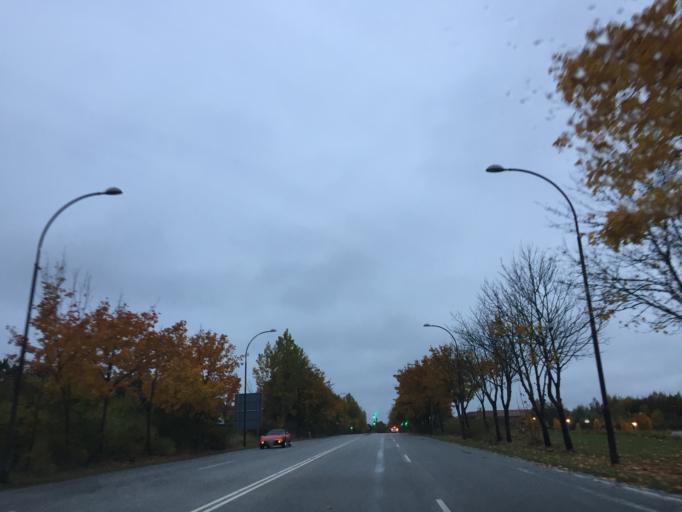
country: DK
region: Zealand
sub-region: Ringsted Kommune
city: Ringsted
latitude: 55.4508
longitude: 11.7864
